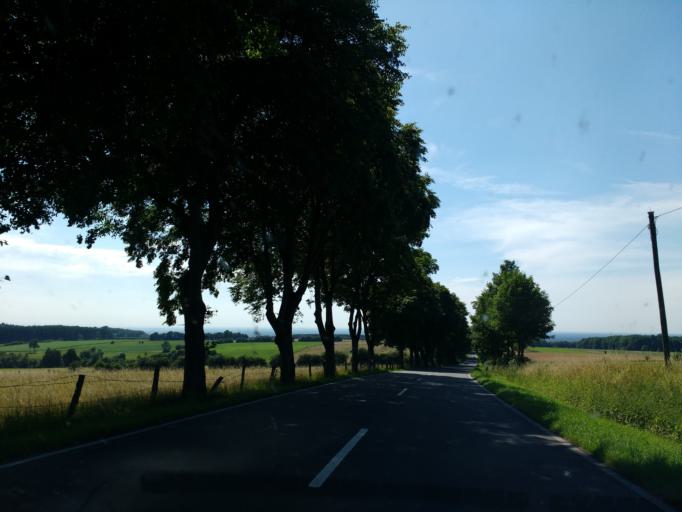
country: DE
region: North Rhine-Westphalia
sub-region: Regierungsbezirk Detmold
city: Schlangen
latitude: 51.8100
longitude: 8.8982
